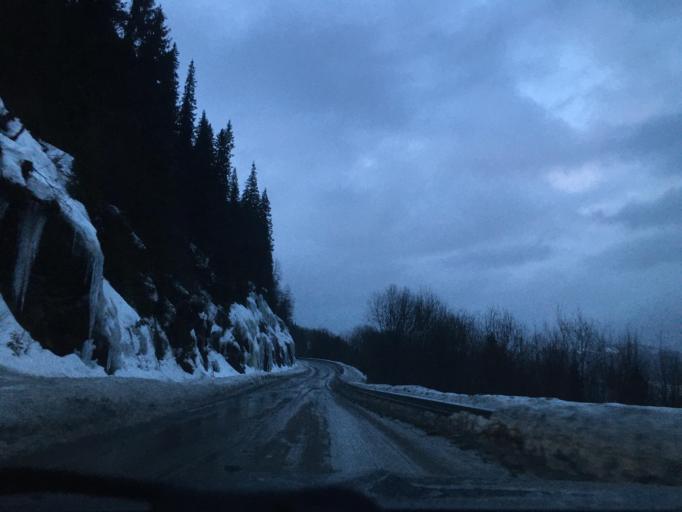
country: NO
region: Nordland
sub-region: Rana
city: Hauknes
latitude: 66.2901
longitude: 13.9123
